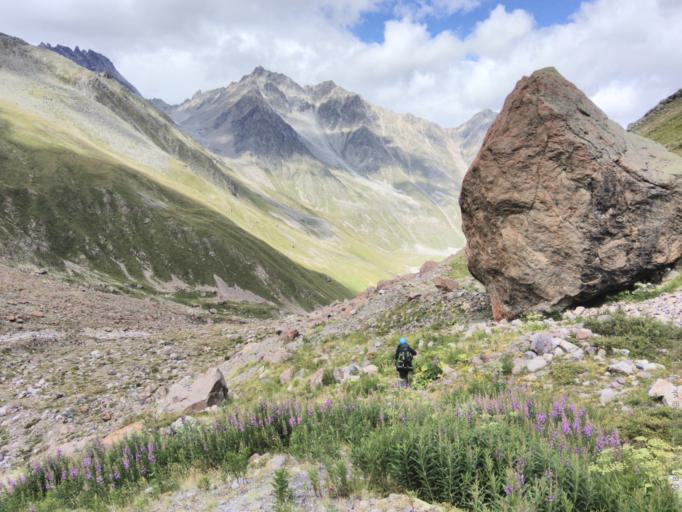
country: RU
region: Kabardino-Balkariya
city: Terskol
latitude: 43.3539
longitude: 42.3532
